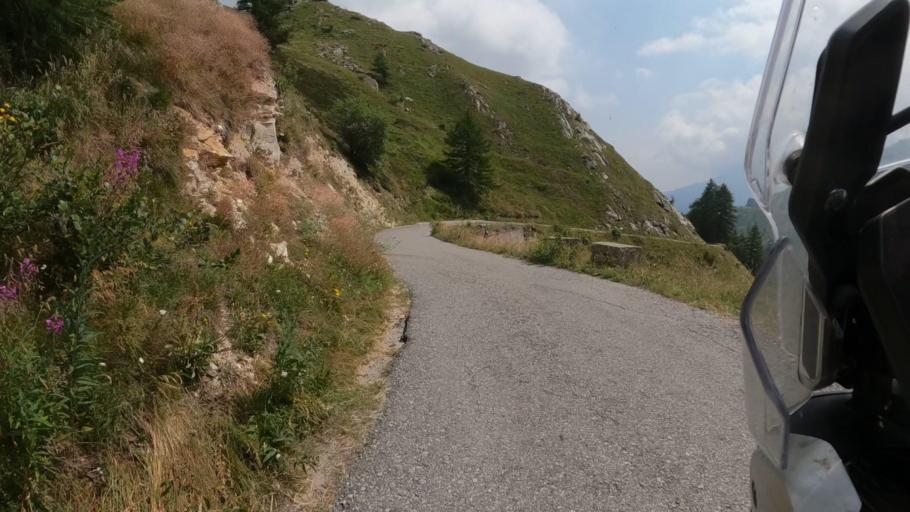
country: IT
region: Piedmont
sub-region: Provincia di Cuneo
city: Campomolino
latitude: 44.3959
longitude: 7.1566
